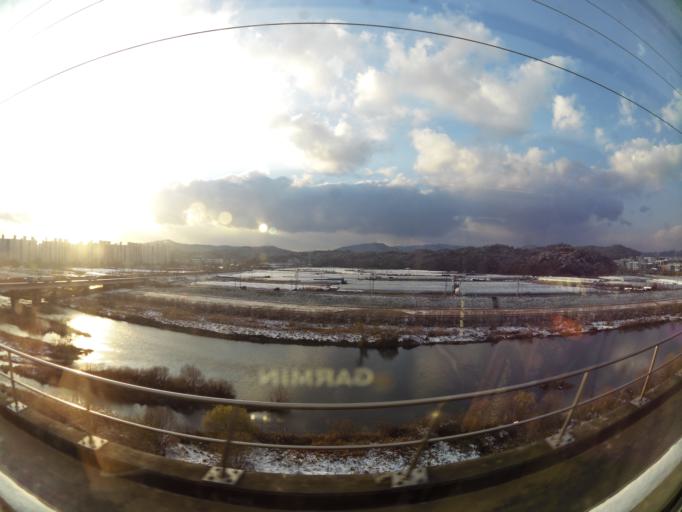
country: KR
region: Daejeon
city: Songgang-dong
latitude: 36.4064
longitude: 127.4150
